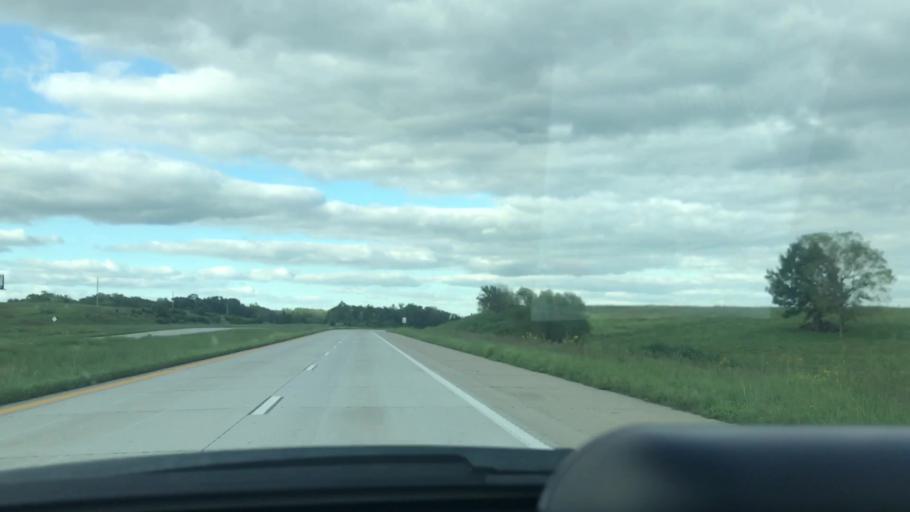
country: US
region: Missouri
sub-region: Benton County
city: Lincoln
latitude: 38.4436
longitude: -93.2942
